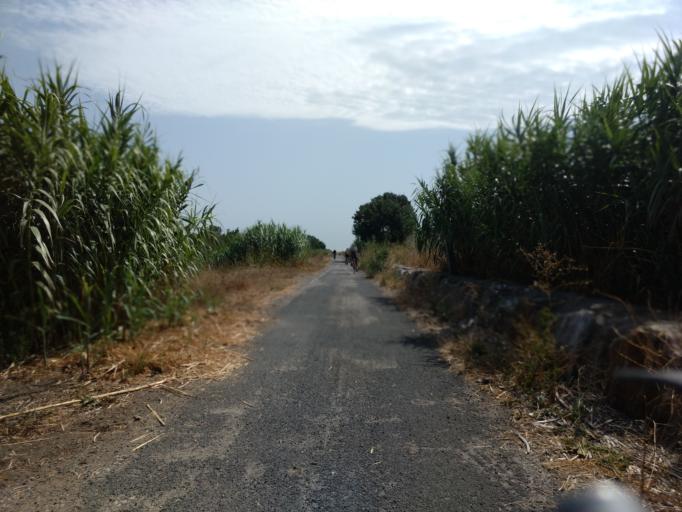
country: FR
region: Languedoc-Roussillon
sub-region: Departement des Pyrenees-Orientales
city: Saint-Laurent-de-la-Salanque
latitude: 42.7641
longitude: 2.9911
